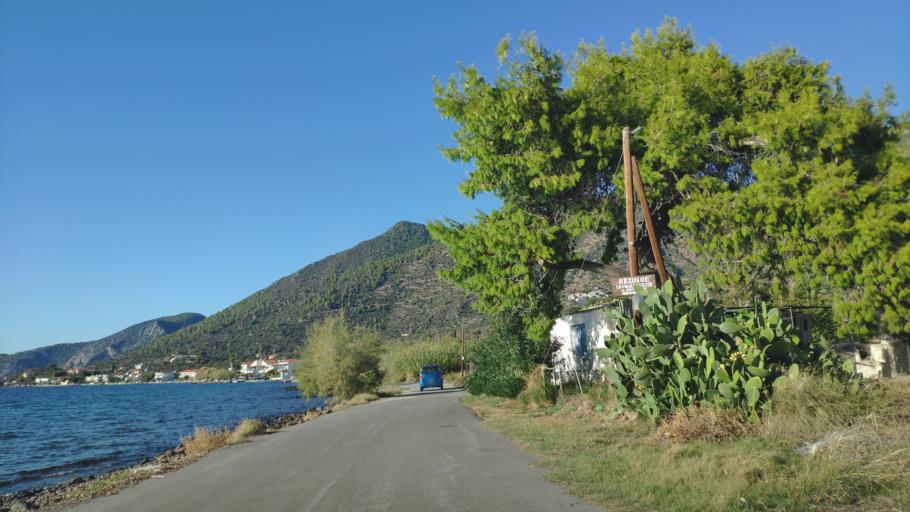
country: GR
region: Attica
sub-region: Nomos Piraios
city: Megalochori
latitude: 37.5843
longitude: 23.3489
